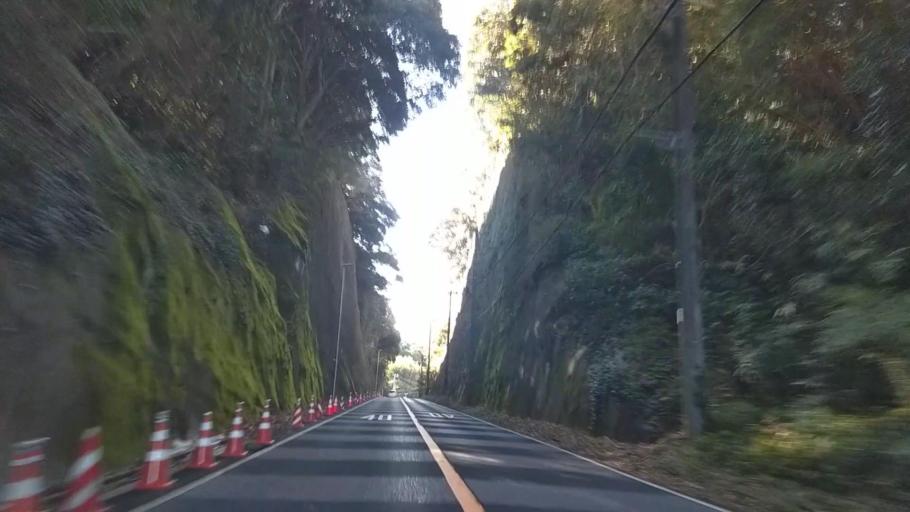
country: JP
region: Chiba
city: Tateyama
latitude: 34.9615
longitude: 139.8549
